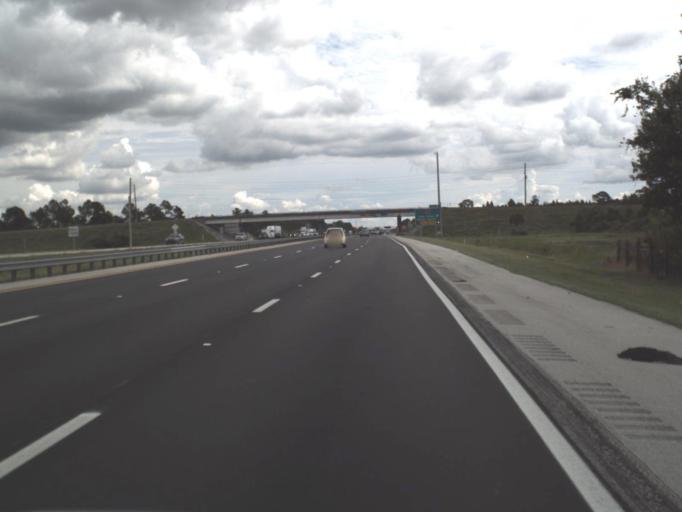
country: US
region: Florida
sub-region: Polk County
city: Polk City
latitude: 28.1809
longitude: -81.7464
